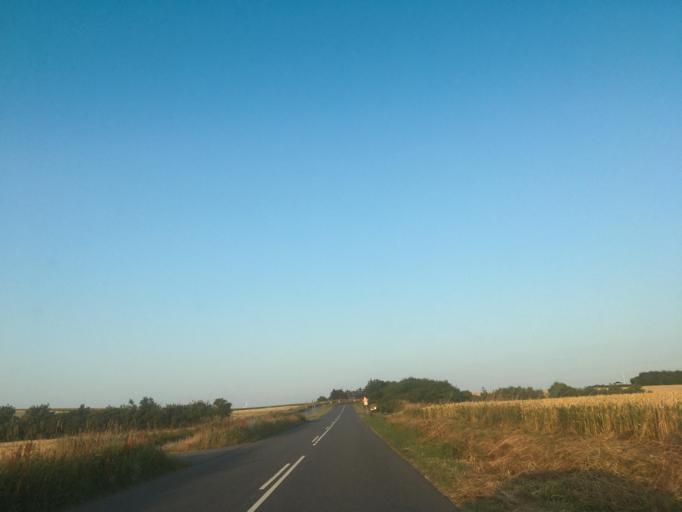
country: DK
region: North Denmark
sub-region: Thisted Kommune
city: Hurup
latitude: 56.7613
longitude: 8.3358
